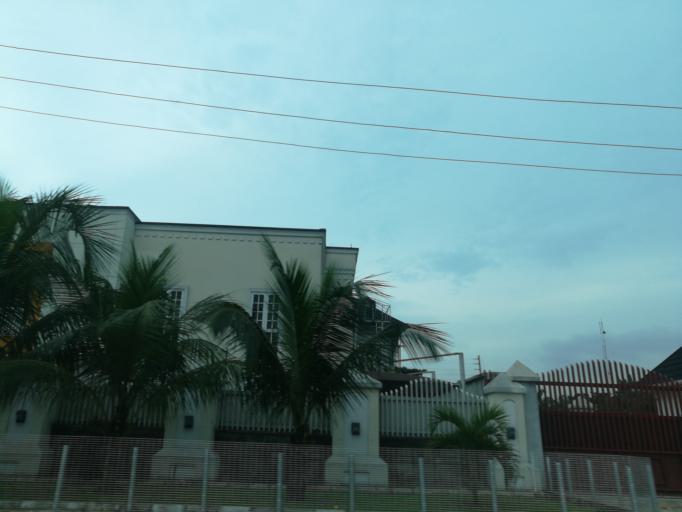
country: NG
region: Rivers
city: Port Harcourt
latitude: 4.8018
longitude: 7.0217
